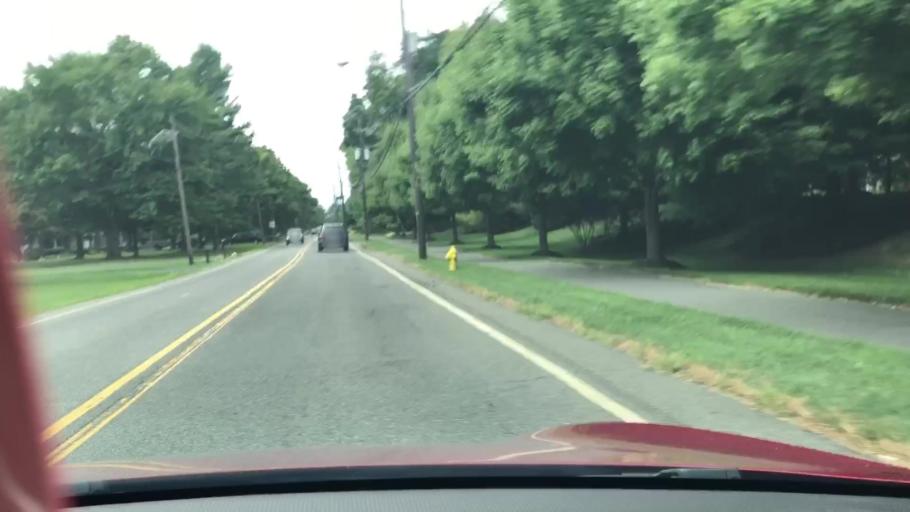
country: US
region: New Jersey
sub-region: Mercer County
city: Robbinsville
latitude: 40.1927
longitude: -74.6305
